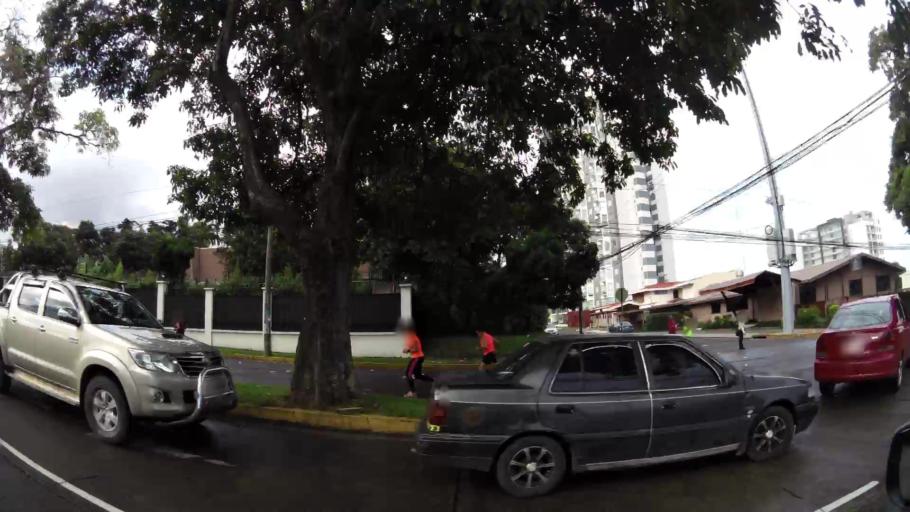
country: CR
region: San Jose
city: Colima
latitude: 9.9404
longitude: -84.1111
